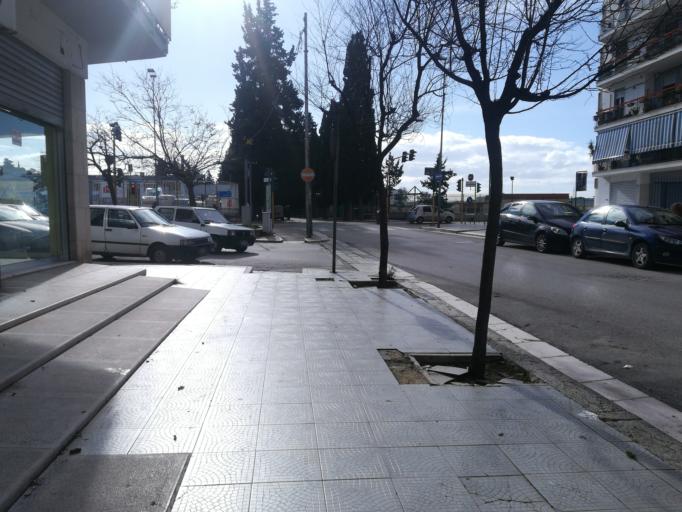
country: IT
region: Apulia
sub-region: Provincia di Barletta - Andria - Trani
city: Andria
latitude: 41.2183
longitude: 16.2994
